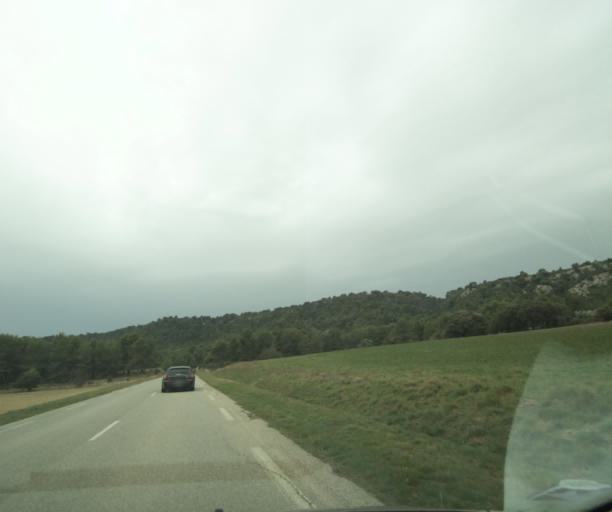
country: FR
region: Provence-Alpes-Cote d'Azur
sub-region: Departement des Bouches-du-Rhone
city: Saint-Marc-Jaumegarde
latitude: 43.5567
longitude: 5.5522
